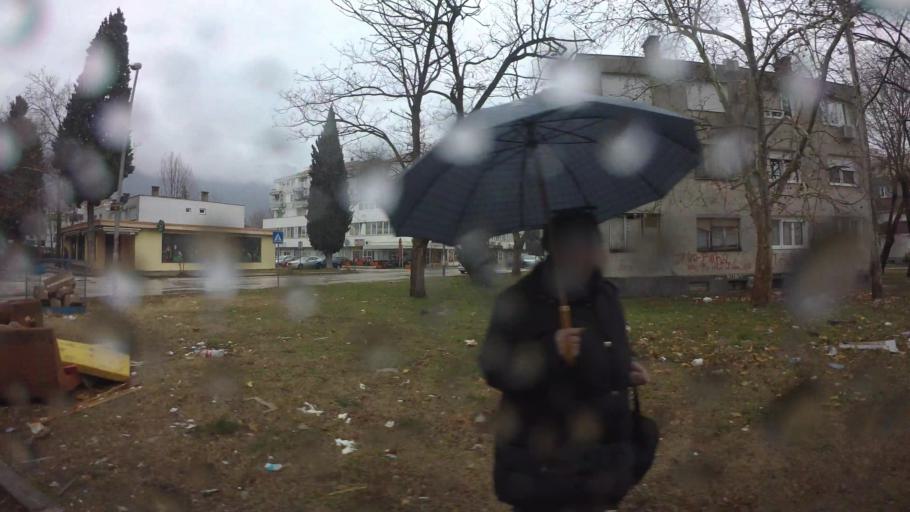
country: BA
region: Federation of Bosnia and Herzegovina
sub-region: Hercegovacko-Bosanski Kanton
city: Mostar
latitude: 43.3517
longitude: 17.7997
